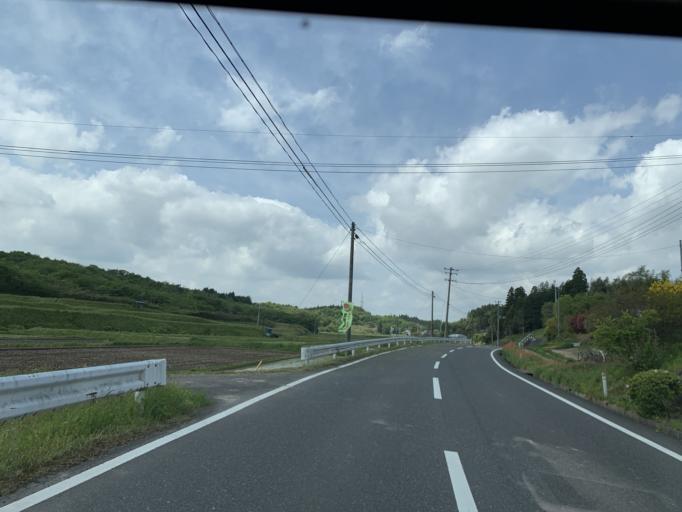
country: JP
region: Iwate
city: Ichinoseki
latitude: 38.7745
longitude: 140.9868
